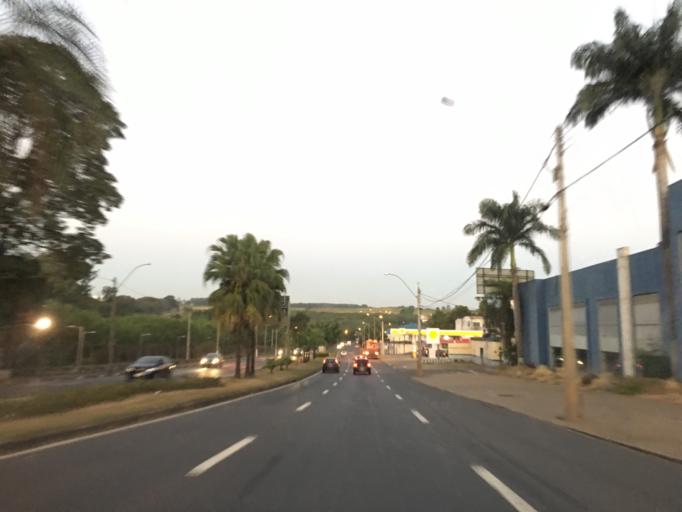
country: BR
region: Sao Paulo
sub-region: Piracicaba
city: Piracicaba
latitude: -22.7158
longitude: -47.6293
